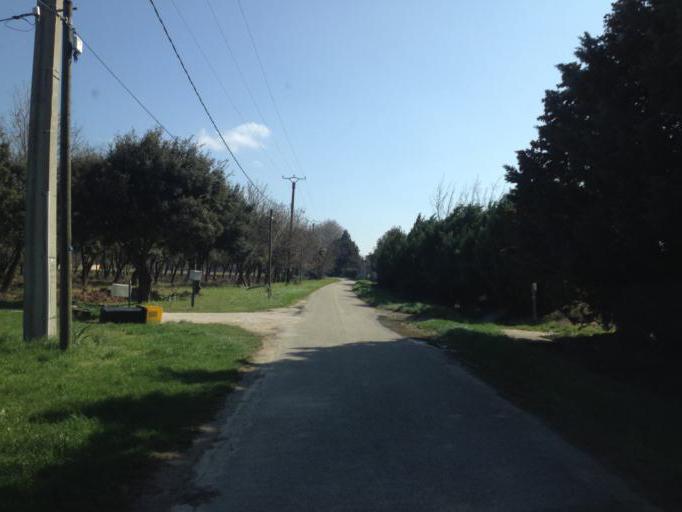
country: FR
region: Provence-Alpes-Cote d'Azur
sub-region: Departement du Vaucluse
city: Jonquieres
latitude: 44.1150
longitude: 4.9176
